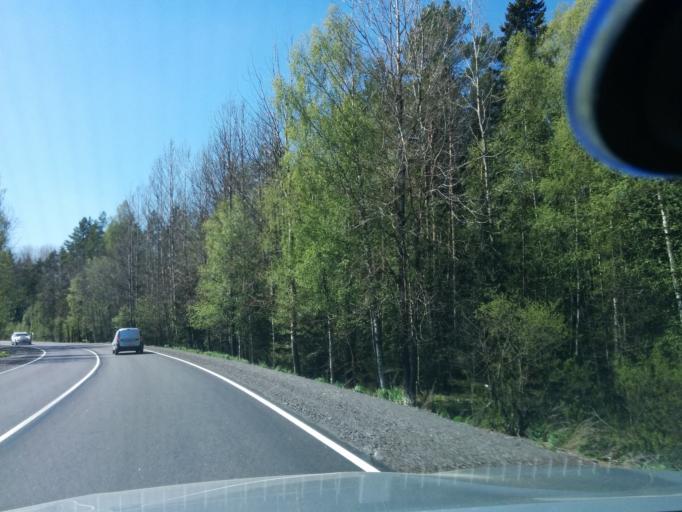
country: RU
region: Leningrad
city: Verkhniye Osel'ki
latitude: 60.1953
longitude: 30.4173
